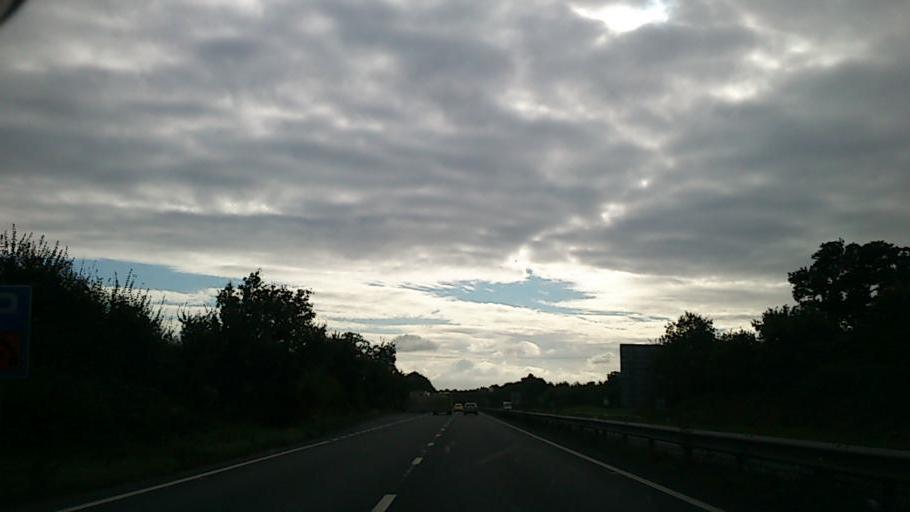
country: GB
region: England
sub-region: Shropshire
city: Great Hanwood
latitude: 52.6894
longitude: -2.8007
